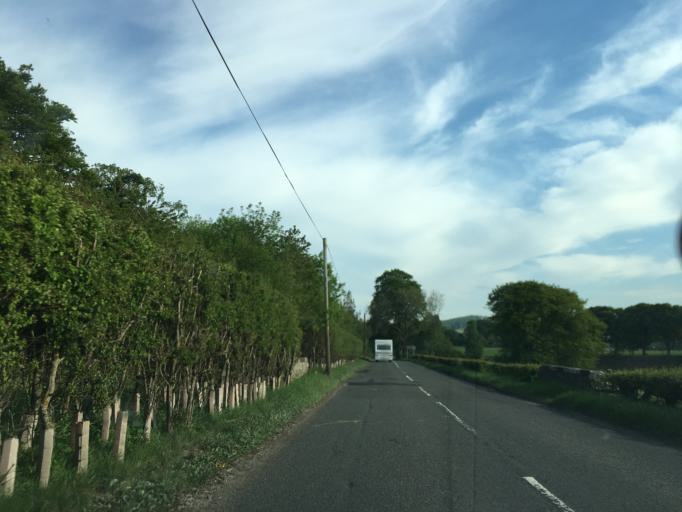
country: GB
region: Scotland
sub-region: South Lanarkshire
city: Biggar
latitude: 55.6214
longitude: -3.4142
